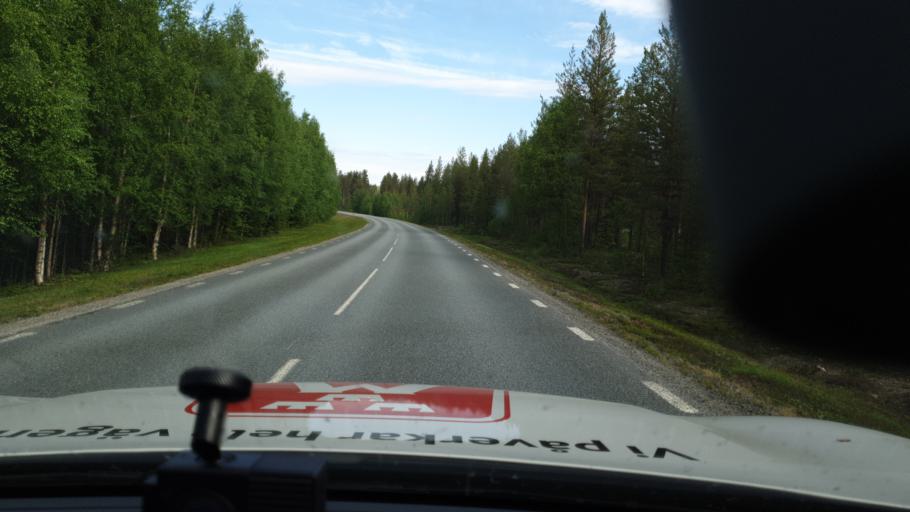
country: SE
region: Vaesterbotten
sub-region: Lycksele Kommun
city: Soderfors
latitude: 65.1687
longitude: 18.2547
